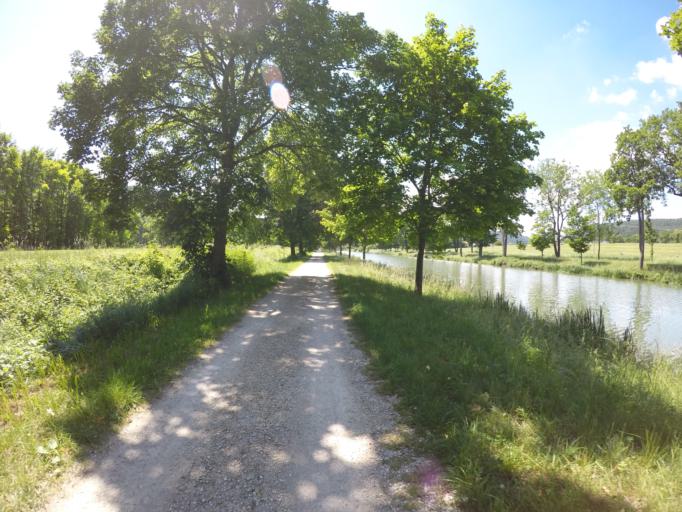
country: DE
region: Bavaria
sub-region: Lower Bavaria
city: Essing
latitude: 48.9257
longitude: 11.8106
